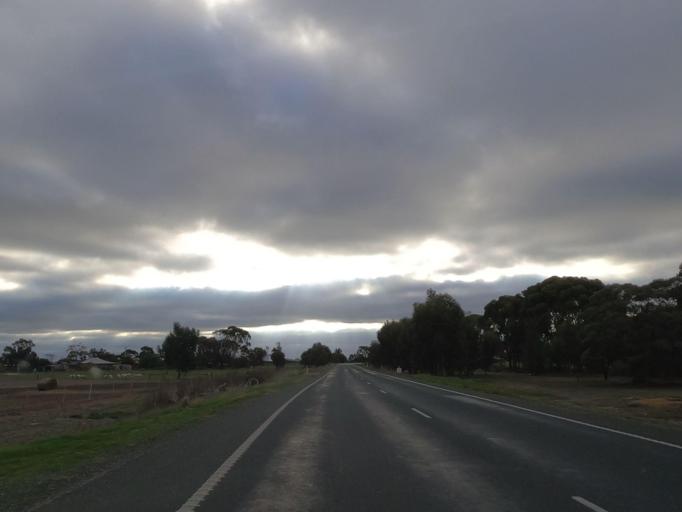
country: AU
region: Victoria
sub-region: Swan Hill
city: Swan Hill
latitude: -35.7317
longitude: 143.8958
